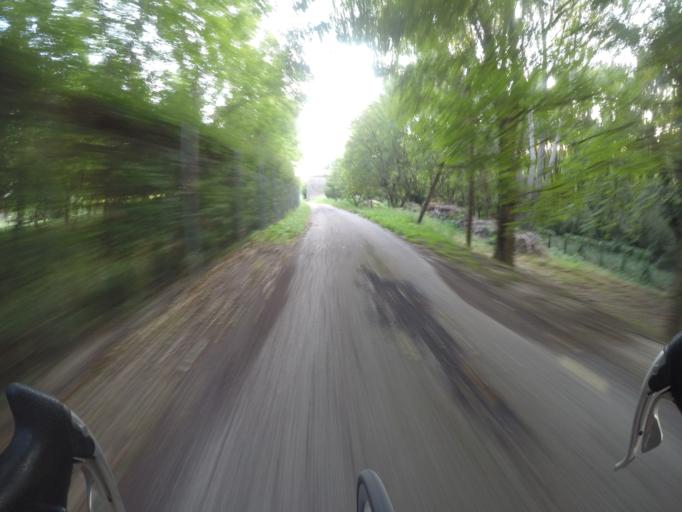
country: IT
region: Veneto
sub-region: Provincia di Rovigo
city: Pincara
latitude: 45.0046
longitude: 11.6256
